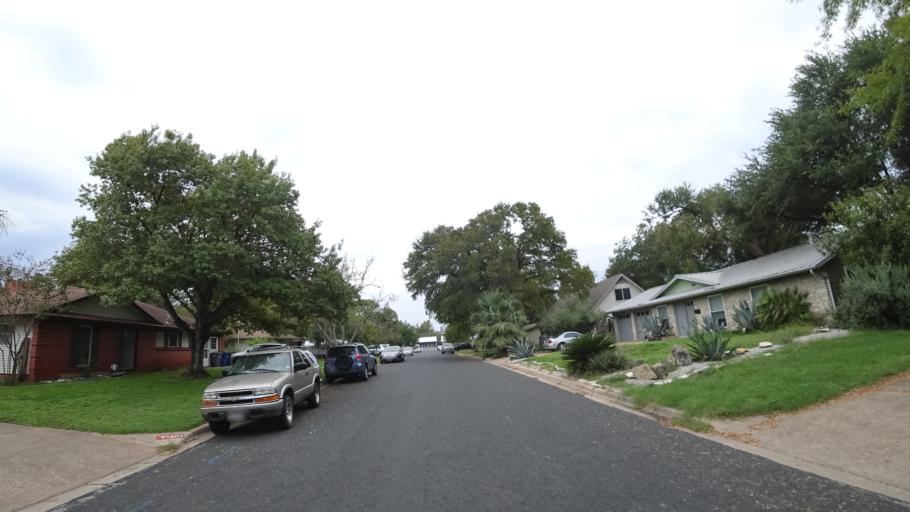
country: US
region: Texas
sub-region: Travis County
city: Rollingwood
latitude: 30.2171
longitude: -97.7944
